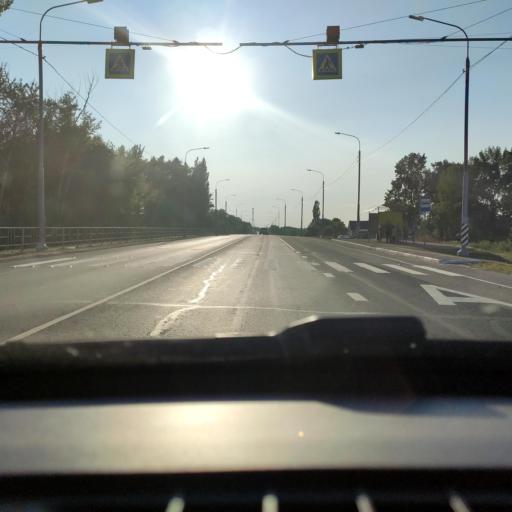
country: RU
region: Voronezj
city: Kashirskoye
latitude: 51.4968
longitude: 39.5936
